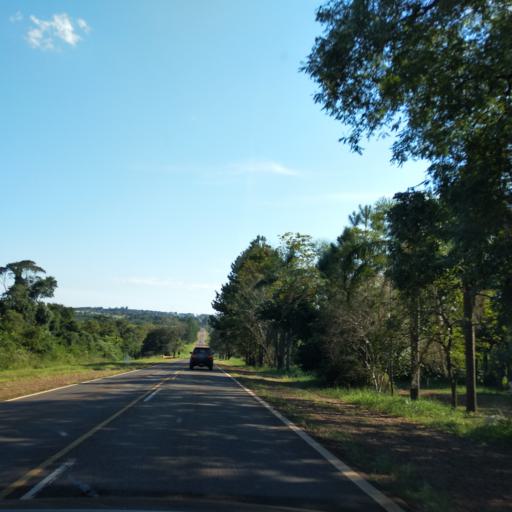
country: AR
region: Misiones
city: Gobernador Roca
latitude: -27.1700
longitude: -55.4462
